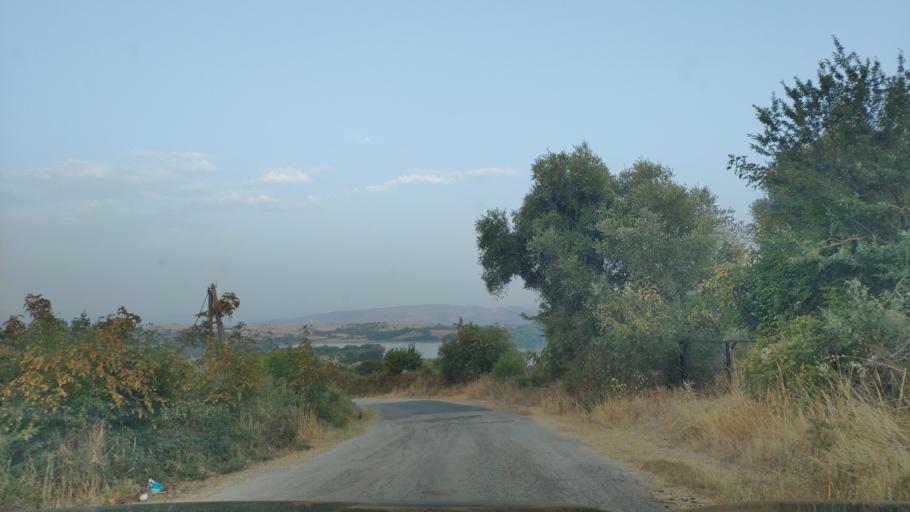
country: GR
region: West Greece
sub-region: Nomos Aitolias kai Akarnanias
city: Monastirakion
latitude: 38.9219
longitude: 20.9848
